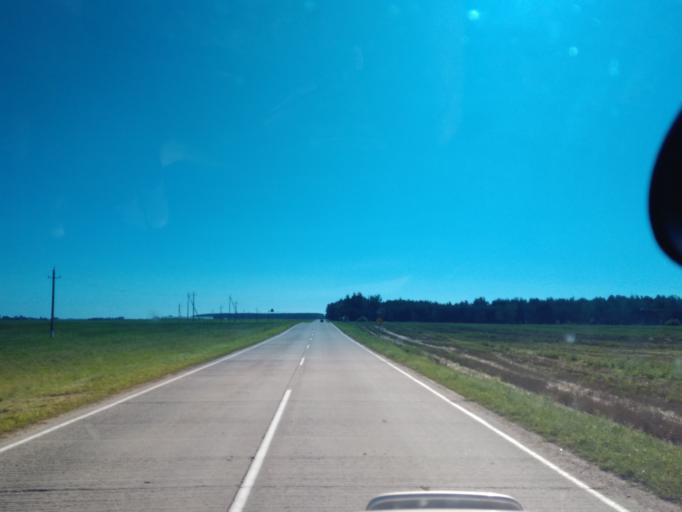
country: BY
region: Minsk
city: Stan'kava
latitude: 53.6265
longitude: 27.2609
